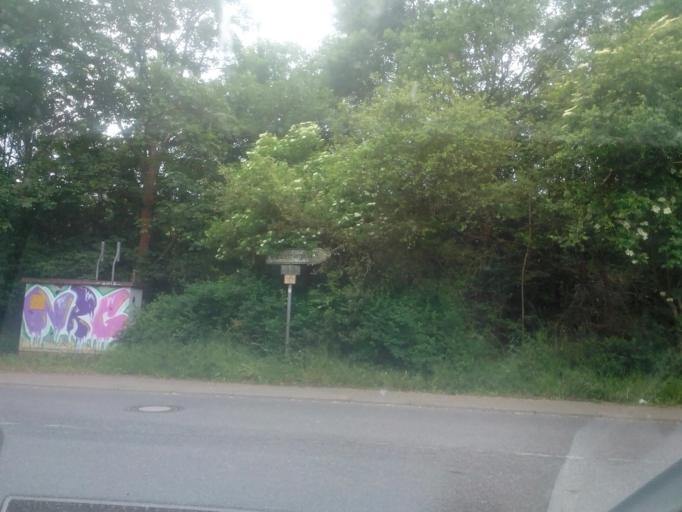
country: DE
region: Saarland
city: Saarlouis
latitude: 49.3082
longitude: 6.7340
